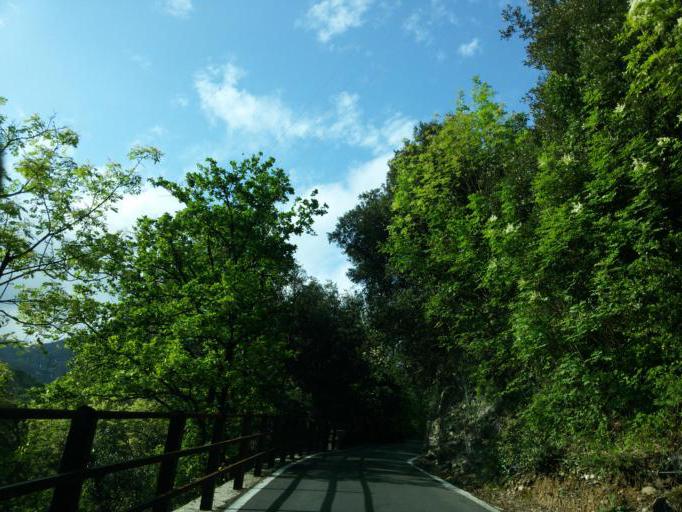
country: IT
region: Liguria
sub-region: Provincia di Genova
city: Piccarello
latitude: 44.4492
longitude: 8.9908
